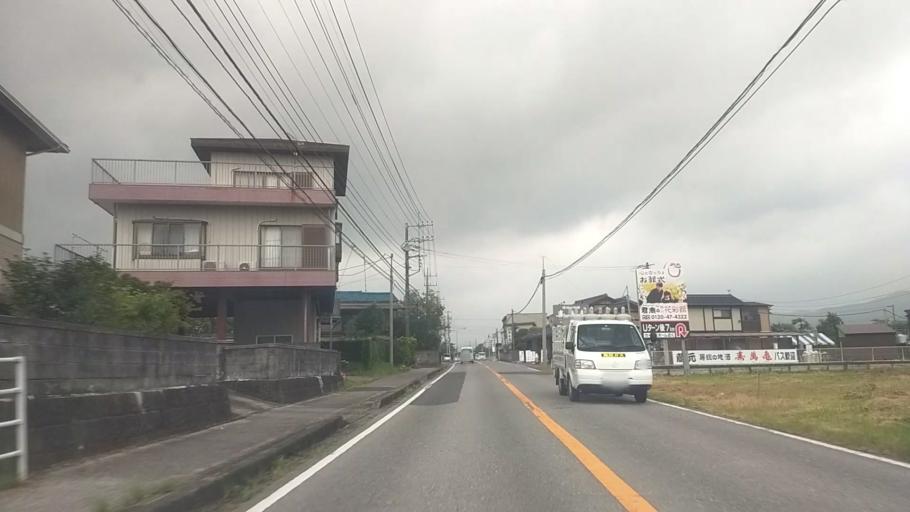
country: JP
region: Chiba
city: Kawaguchi
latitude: 35.1307
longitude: 140.0248
